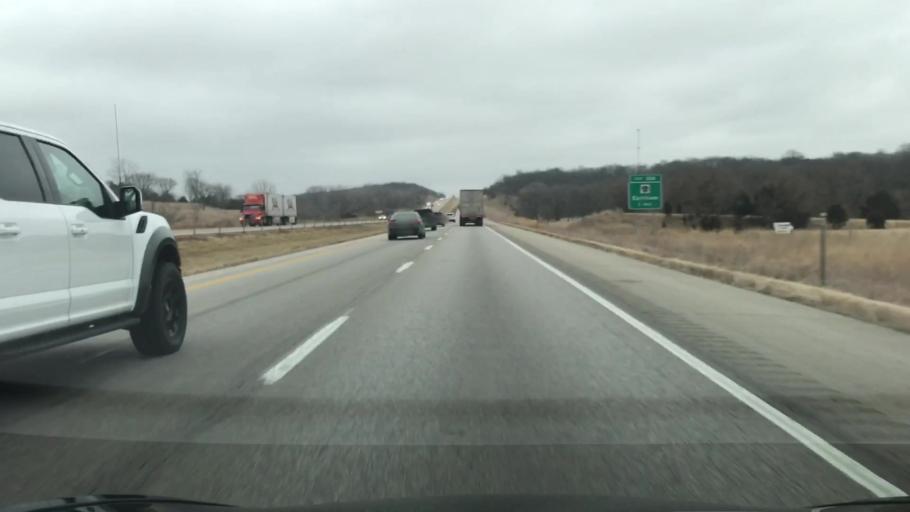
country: US
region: Iowa
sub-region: Madison County
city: Earlham
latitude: 41.5176
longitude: -94.1483
